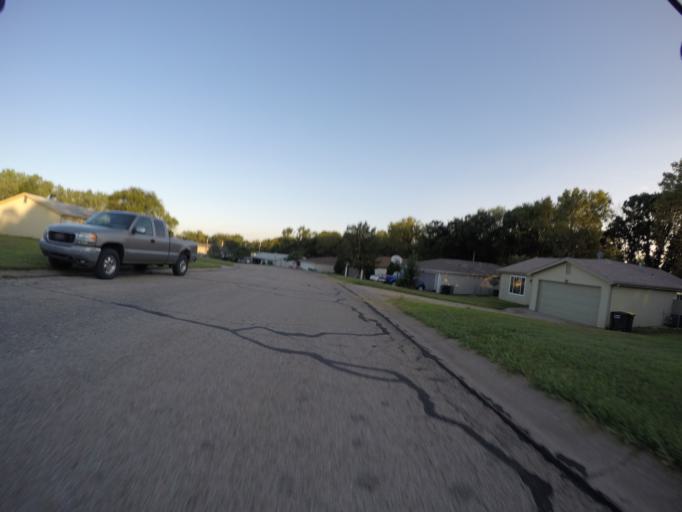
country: US
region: Kansas
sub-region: Riley County
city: Ogden
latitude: 39.1208
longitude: -96.7126
